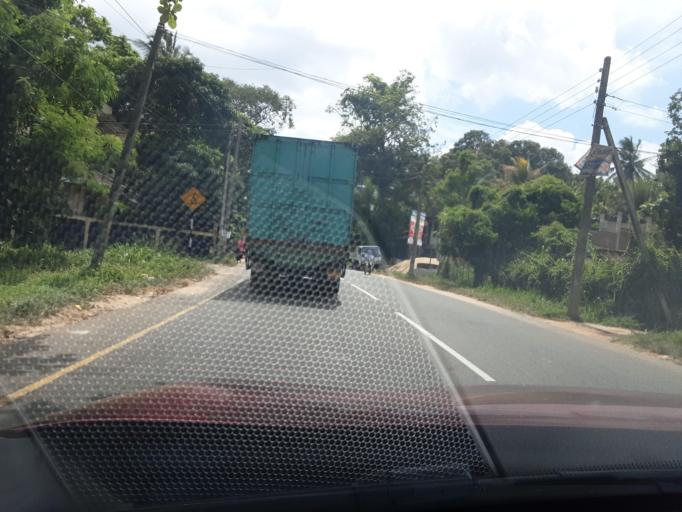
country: LK
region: North Western
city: Kuliyapitiya
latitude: 7.4504
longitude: 80.1957
